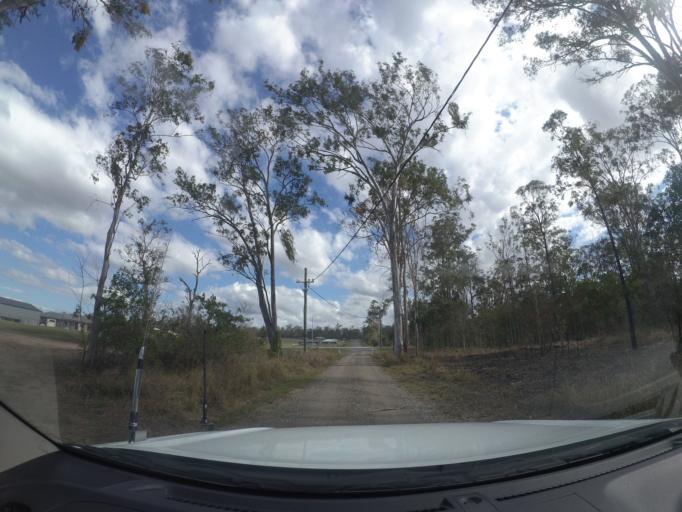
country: AU
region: Queensland
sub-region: Logan
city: North Maclean
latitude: -27.8101
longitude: 152.9930
